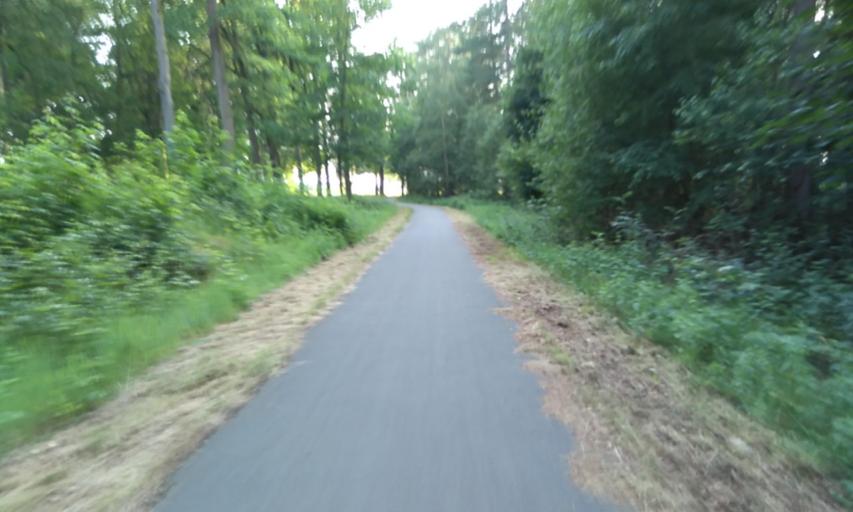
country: DE
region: Lower Saxony
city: Beckdorf
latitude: 53.4249
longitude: 9.5763
